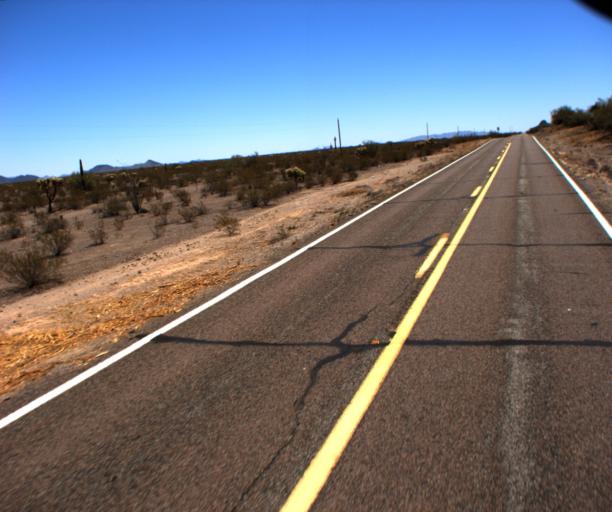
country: US
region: Arizona
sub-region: Pima County
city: Ajo
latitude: 32.2081
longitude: -112.5986
